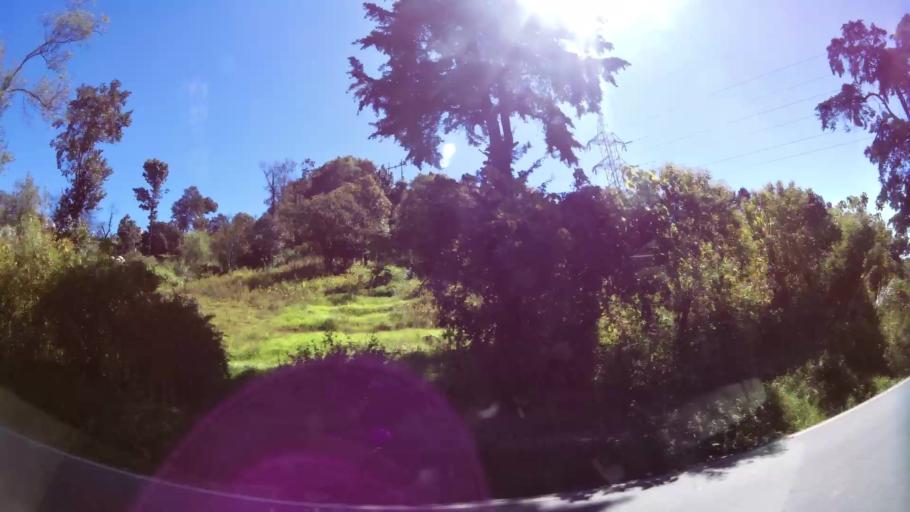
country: GT
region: Solola
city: Solola
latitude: 14.7626
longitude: -91.1775
